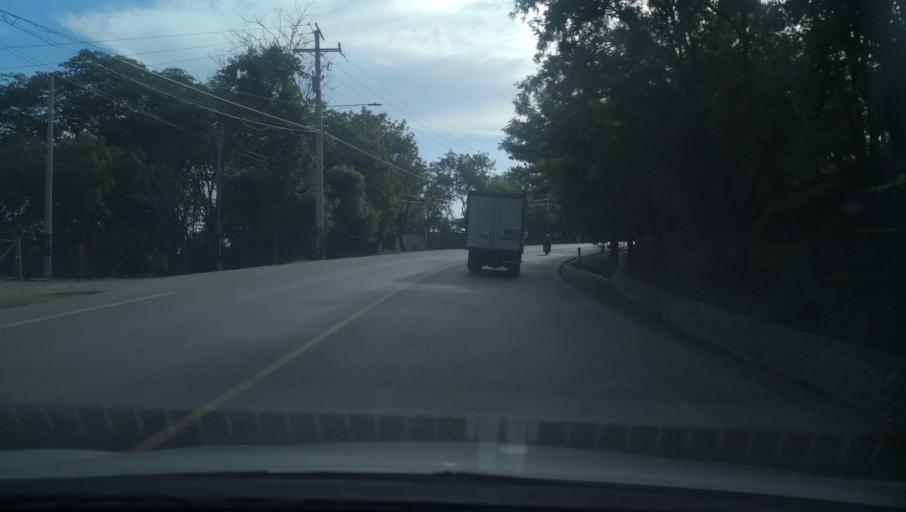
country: NI
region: Nueva Segovia
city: Ocotal
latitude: 13.6133
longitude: -86.4719
